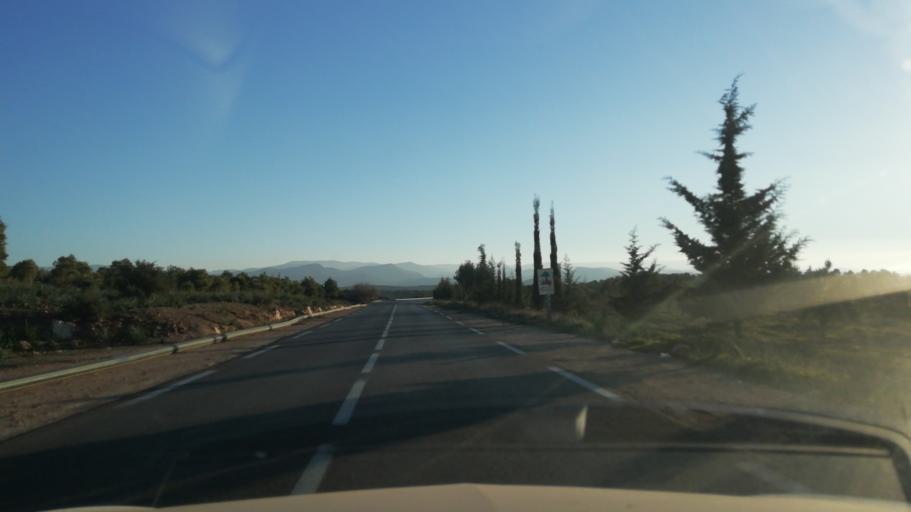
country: DZ
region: Tlemcen
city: Beni Mester
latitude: 34.8185
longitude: -1.6146
